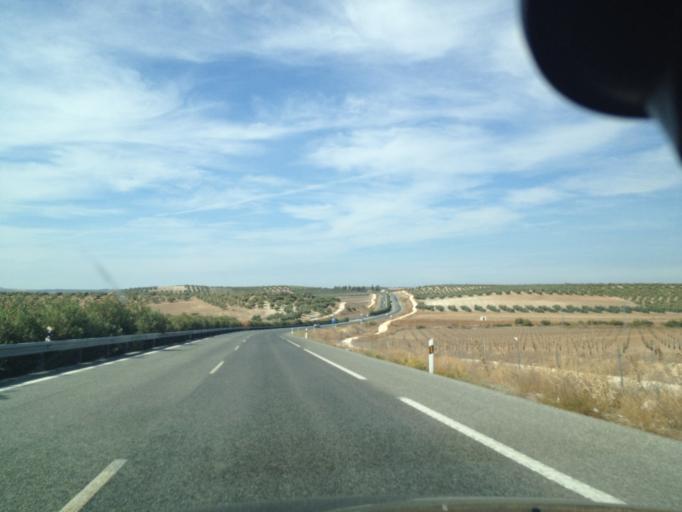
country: ES
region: Andalusia
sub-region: Provincia de Sevilla
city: La Puebla de Cazalla
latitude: 37.2316
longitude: -5.2393
